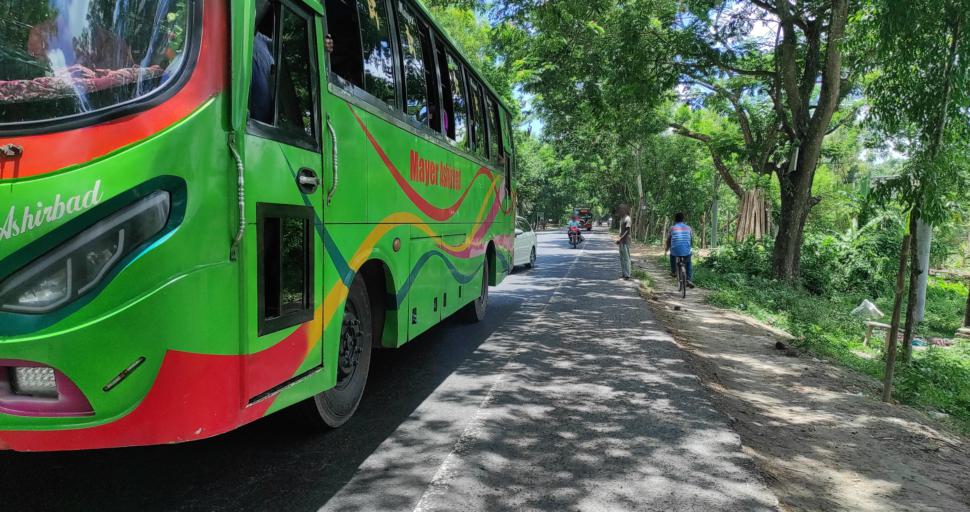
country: BD
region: Barisal
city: Gaurnadi
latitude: 22.8302
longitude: 90.2575
